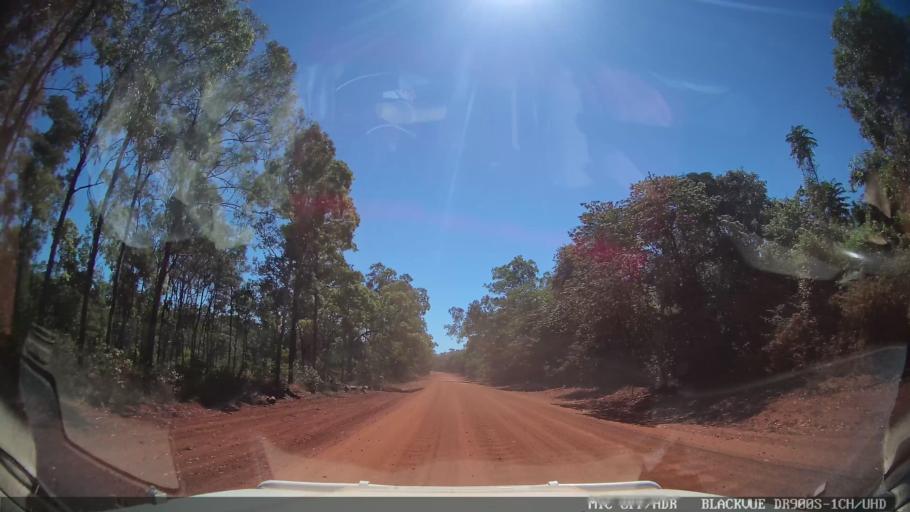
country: AU
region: Queensland
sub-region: Torres
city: Thursday Island
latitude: -10.8892
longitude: 142.4009
